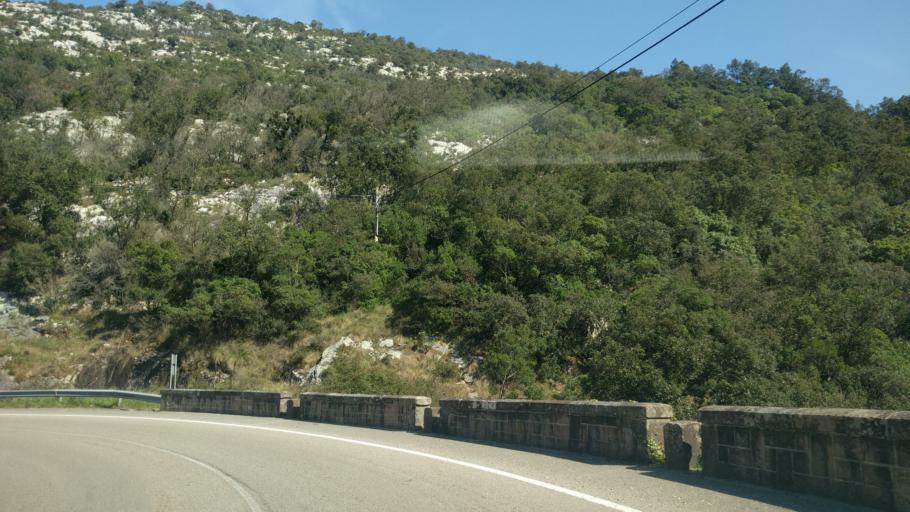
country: ES
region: Cantabria
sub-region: Provincia de Cantabria
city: San Vicente de la Barquera
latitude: 43.2676
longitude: -4.4125
